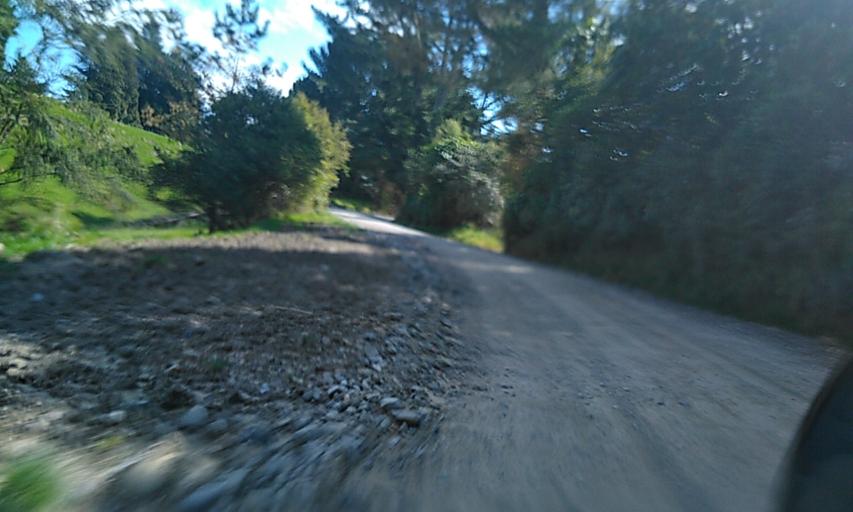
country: NZ
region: Gisborne
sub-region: Gisborne District
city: Gisborne
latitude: -38.2037
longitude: 178.0609
